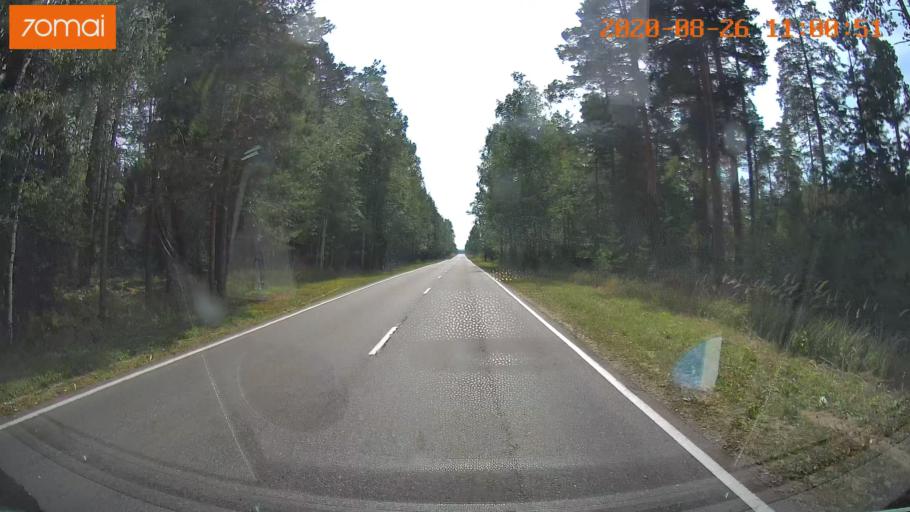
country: RU
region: Rjazan
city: Izhevskoye
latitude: 54.5703
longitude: 41.2175
